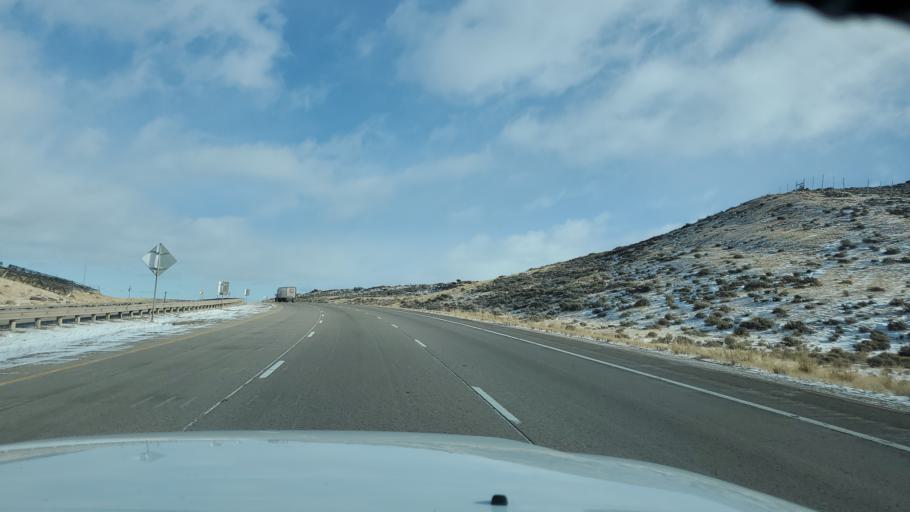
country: US
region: Wyoming
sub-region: Uinta County
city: Evanston
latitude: 41.2945
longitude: -110.6872
